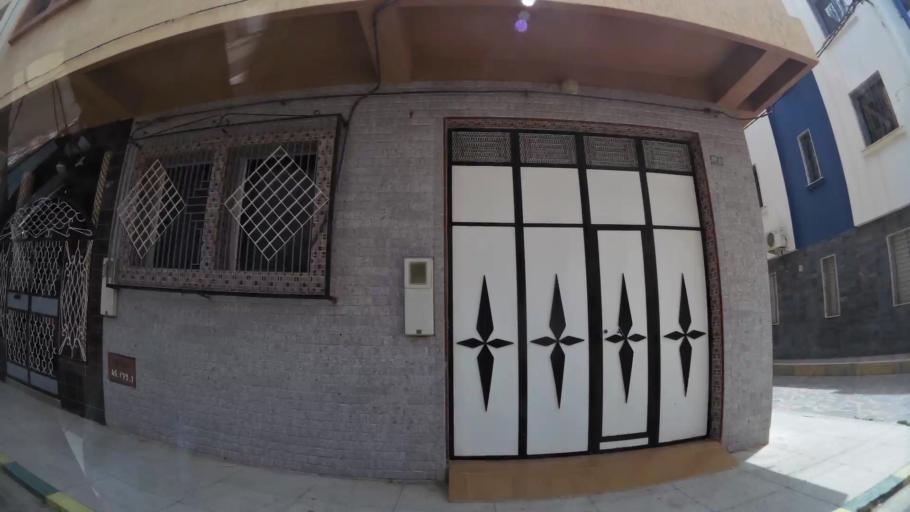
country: MA
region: Oriental
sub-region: Nador
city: Nador
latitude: 35.1672
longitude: -2.9239
